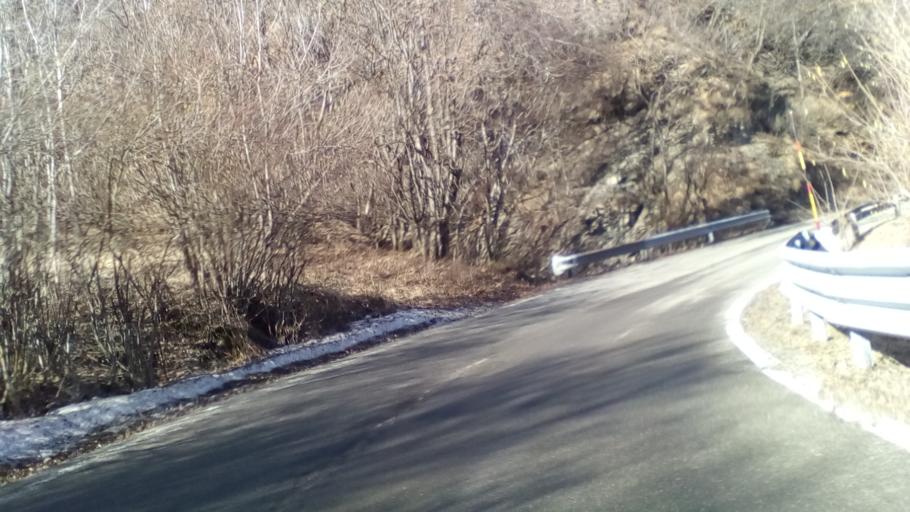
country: IT
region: Emilia-Romagna
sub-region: Provincia di Modena
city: Riolunato
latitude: 44.2493
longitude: 10.6319
